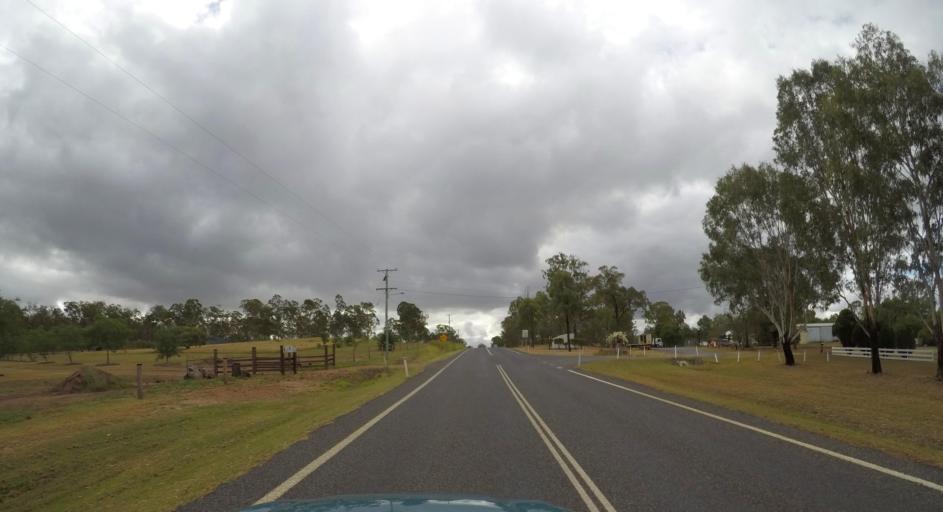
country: AU
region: Queensland
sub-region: North Burnett
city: Gayndah
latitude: -25.3629
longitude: 151.1199
